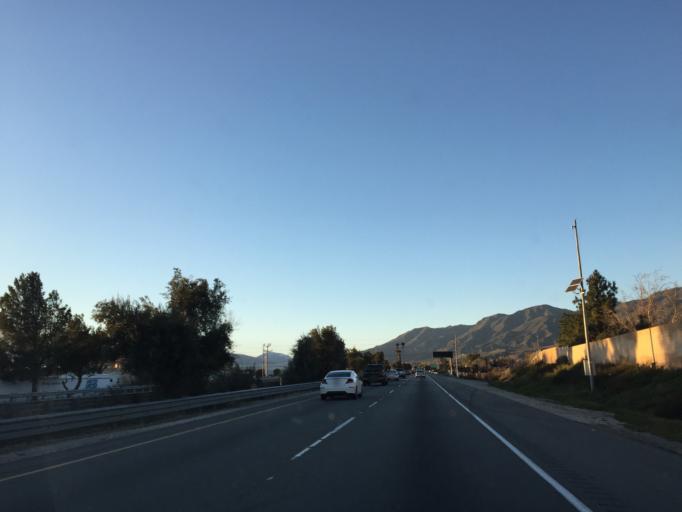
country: US
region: California
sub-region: San Bernardino County
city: Muscoy
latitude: 34.1757
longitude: -117.3429
